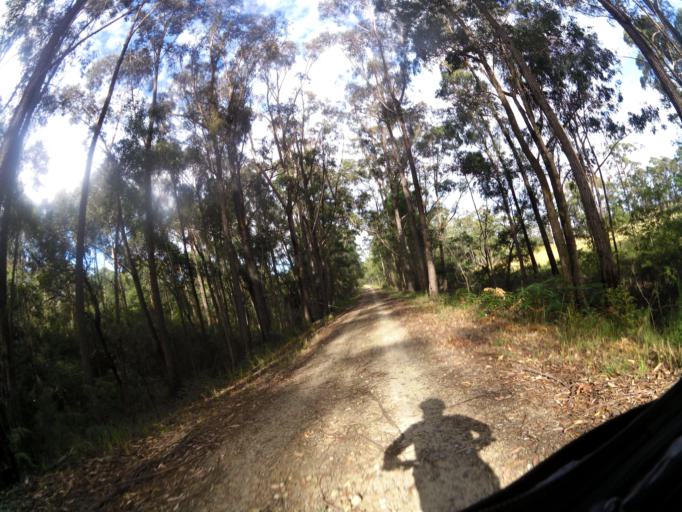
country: AU
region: Victoria
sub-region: East Gippsland
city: Lakes Entrance
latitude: -37.7449
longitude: 148.3897
